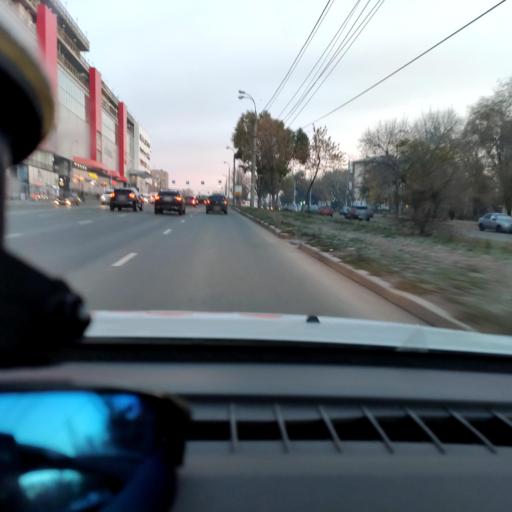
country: RU
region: Samara
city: Samara
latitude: 53.1894
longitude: 50.1912
